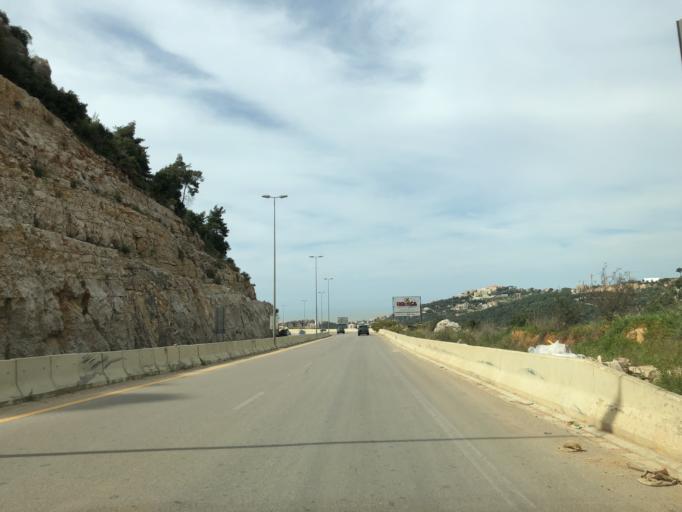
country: LB
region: Mont-Liban
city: Jdaidet el Matn
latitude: 33.8978
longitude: 35.6479
